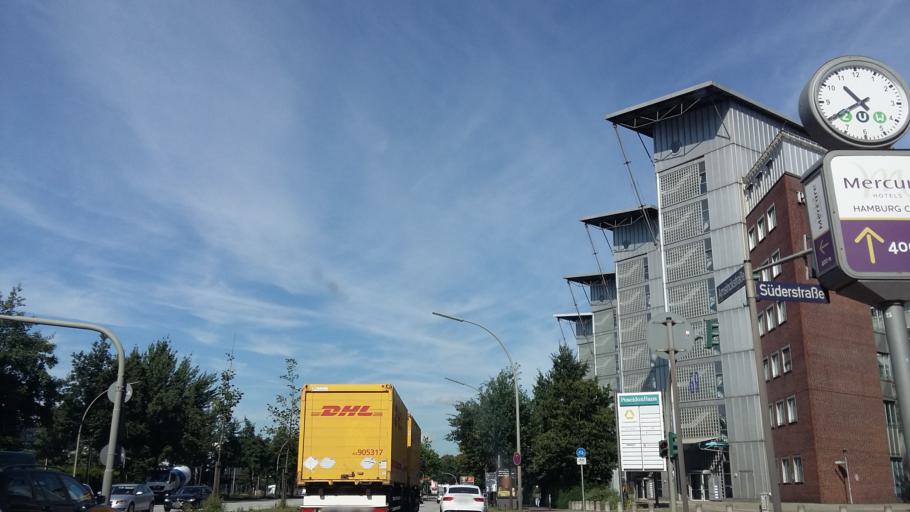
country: DE
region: Hamburg
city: Hammerbrook
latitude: 53.5428
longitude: 10.0252
